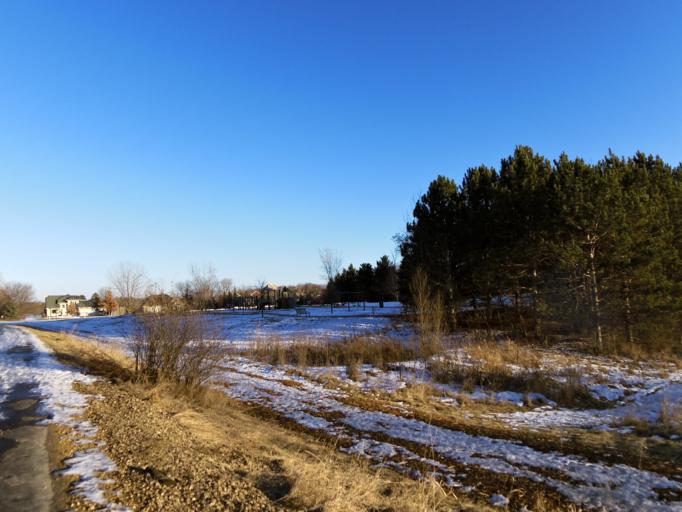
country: US
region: Minnesota
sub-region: Washington County
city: Stillwater
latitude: 45.0699
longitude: -92.8455
